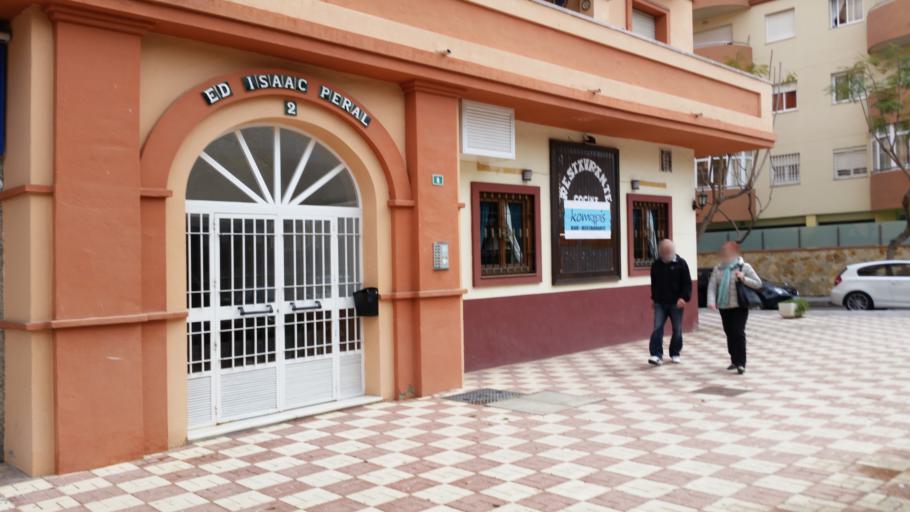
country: ES
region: Andalusia
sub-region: Provincia de Malaga
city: Fuengirola
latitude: 36.5503
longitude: -4.6177
